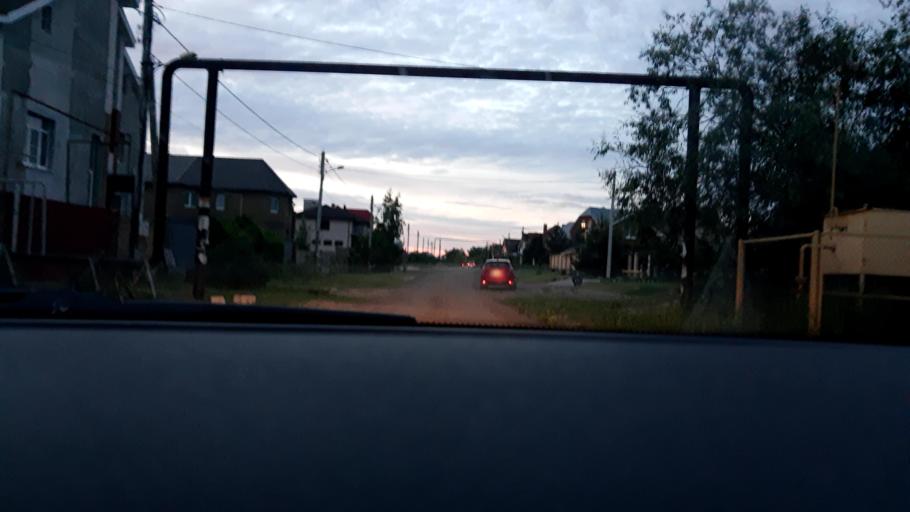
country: RU
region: Nizjnij Novgorod
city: Gorbatovka
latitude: 56.3839
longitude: 43.7649
